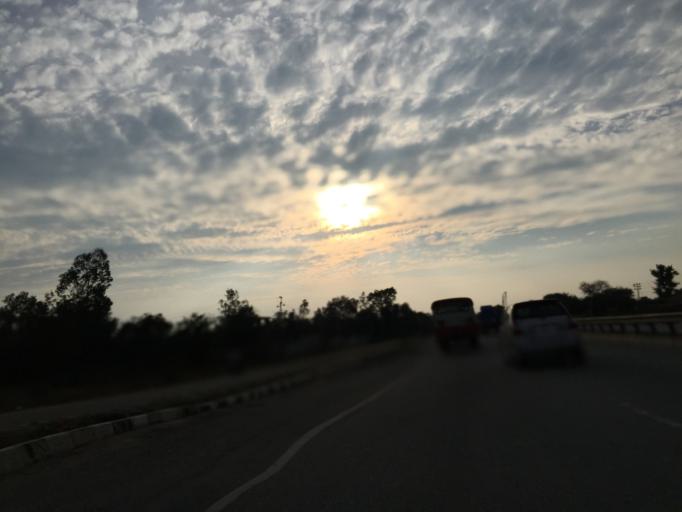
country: IN
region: Karnataka
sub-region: Kolar
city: Kolar
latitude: 13.1409
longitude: 78.2271
